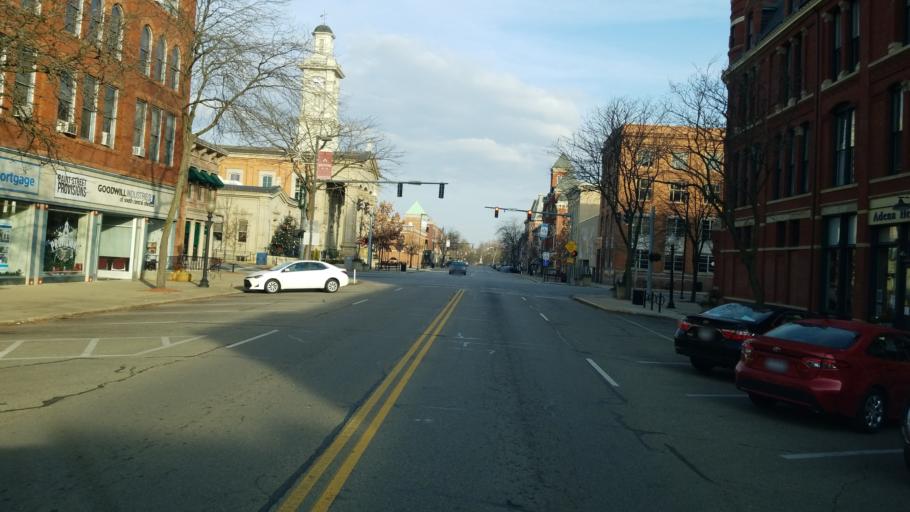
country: US
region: Ohio
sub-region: Ross County
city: Chillicothe
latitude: 39.3327
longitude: -82.9820
